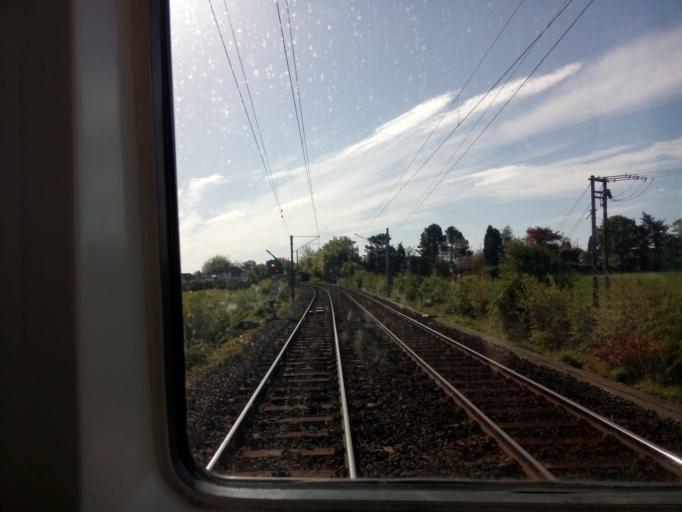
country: GB
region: England
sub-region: Newcastle upon Tyne
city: Dinnington
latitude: 55.0148
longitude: -1.6819
